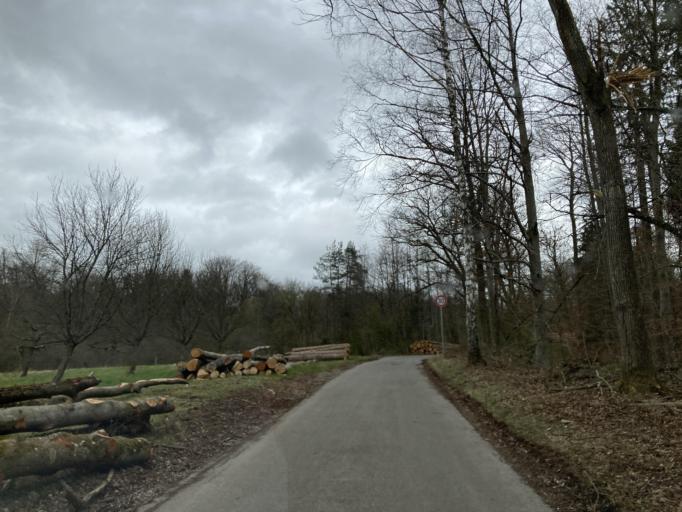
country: DE
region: Baden-Wuerttemberg
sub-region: Tuebingen Region
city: Tuebingen
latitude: 48.4917
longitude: 9.0776
